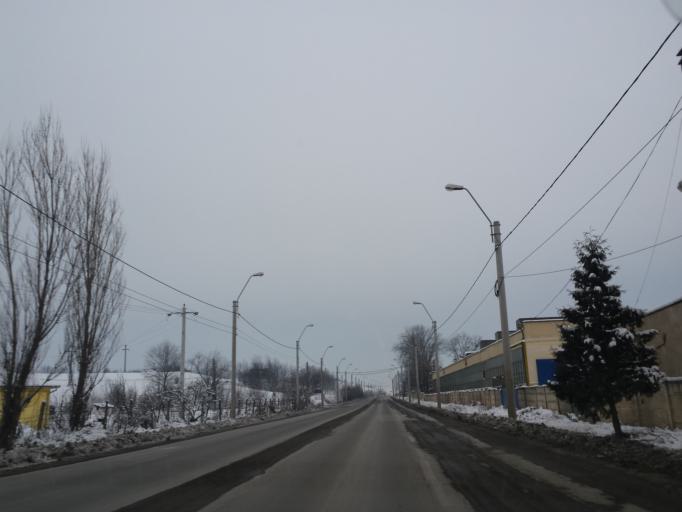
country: RO
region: Hunedoara
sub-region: Municipiul Deva
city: Cristur
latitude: 45.8373
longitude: 22.9473
